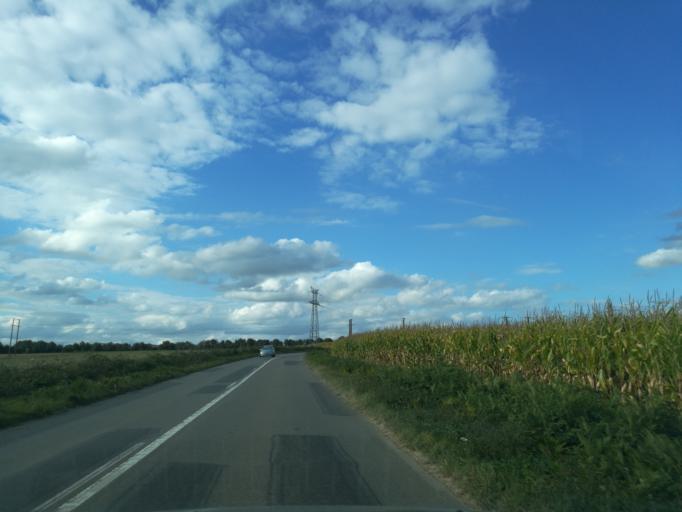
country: FR
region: Brittany
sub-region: Departement d'Ille-et-Vilaine
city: Montfort-sur-Meu
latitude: 48.1462
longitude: -1.9483
